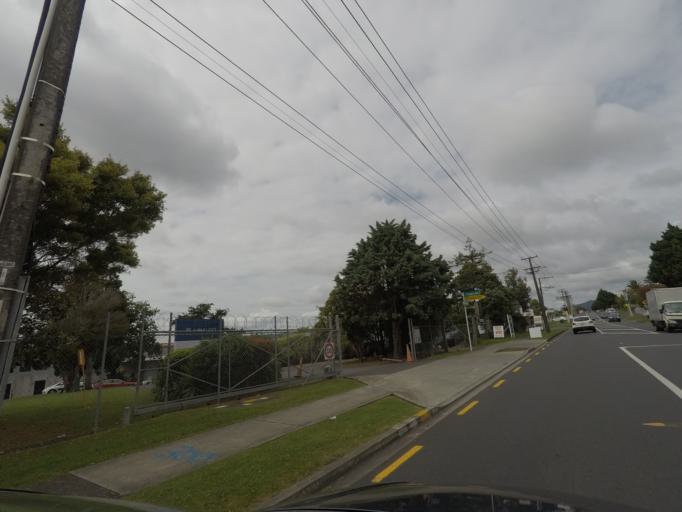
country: NZ
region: Auckland
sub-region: Auckland
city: Waitakere
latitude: -36.8937
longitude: 174.6290
